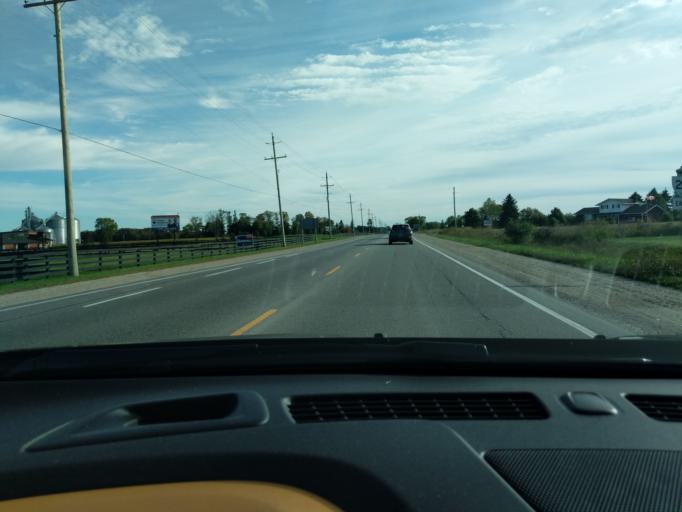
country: CA
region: Ontario
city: Wasaga Beach
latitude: 44.4506
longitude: -80.1030
